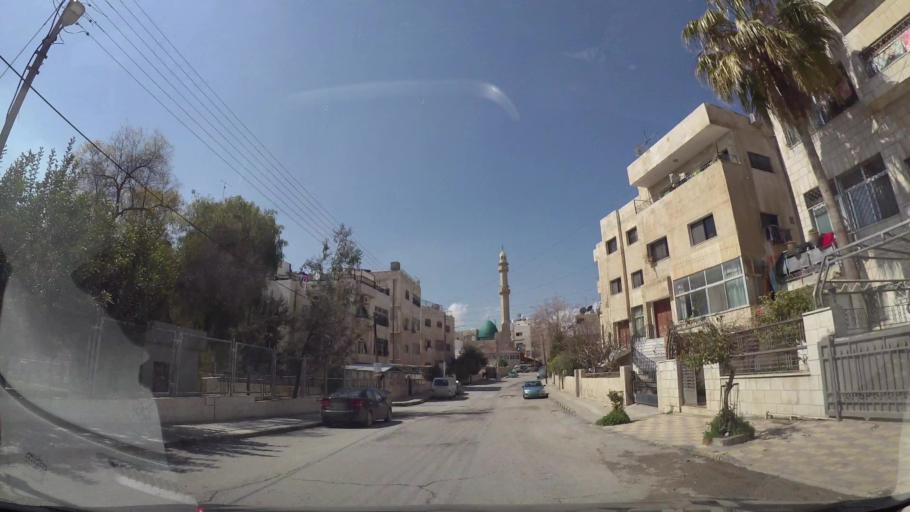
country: JO
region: Amman
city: Amman
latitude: 31.9768
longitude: 35.9922
